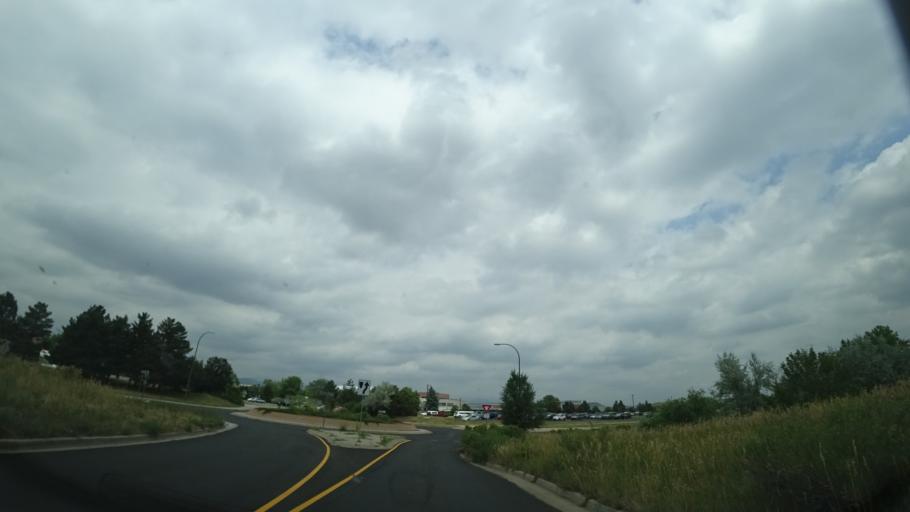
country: US
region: Colorado
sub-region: Jefferson County
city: West Pleasant View
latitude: 39.7187
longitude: -105.1479
